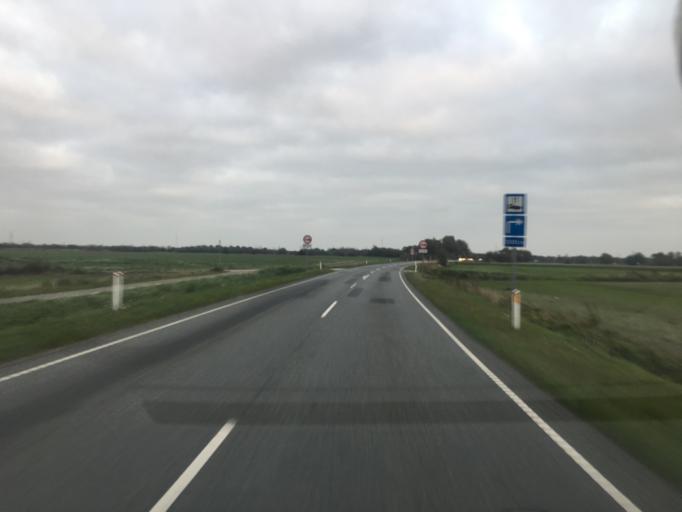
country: DK
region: South Denmark
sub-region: Tonder Kommune
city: Tonder
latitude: 54.9494
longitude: 8.8305
